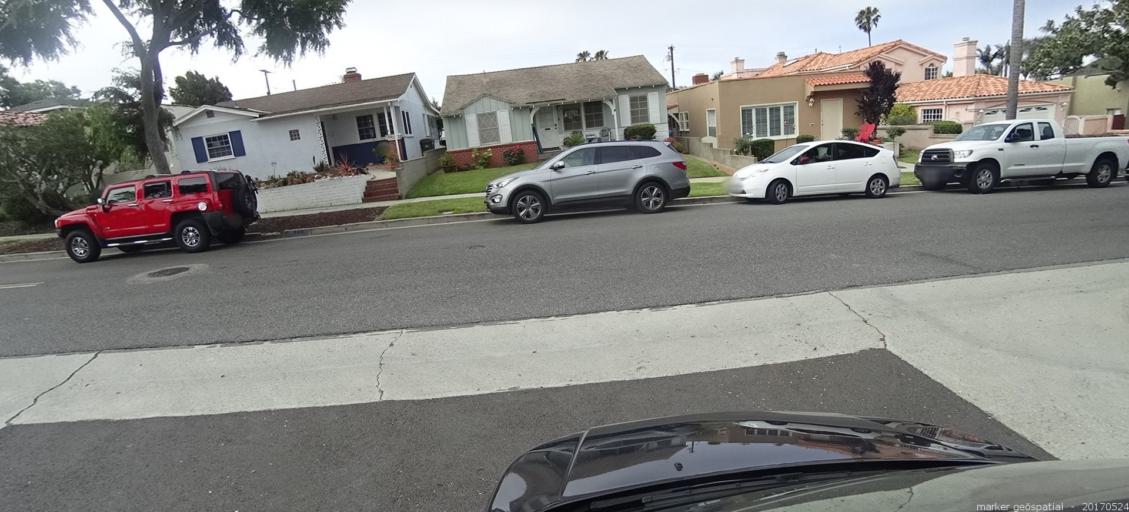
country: US
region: California
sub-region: Los Angeles County
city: Redondo Beach
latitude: 33.8263
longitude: -118.3798
